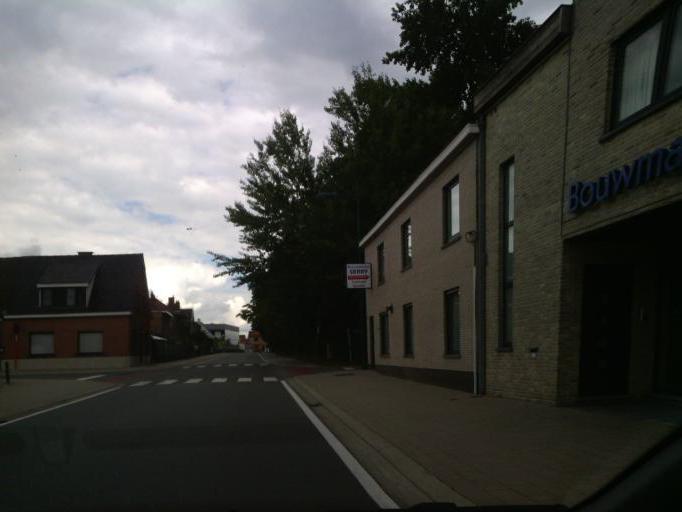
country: BE
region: Flanders
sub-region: Provincie Oost-Vlaanderen
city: Aalter
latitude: 51.0450
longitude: 3.4648
